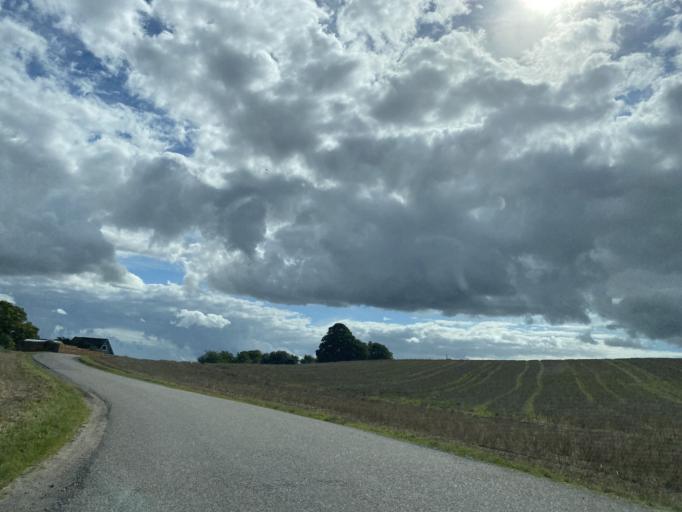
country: DK
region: Central Jutland
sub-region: Skanderborg Kommune
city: Skanderborg
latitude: 55.9763
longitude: 9.8558
